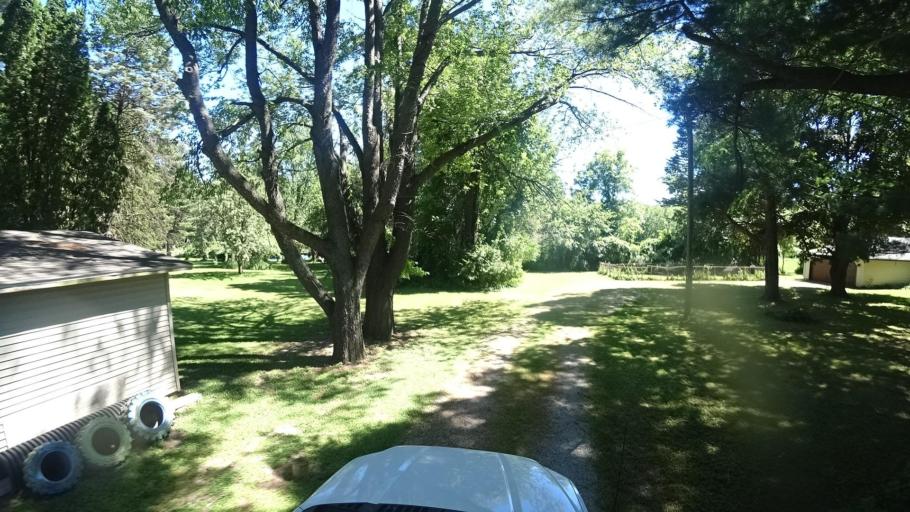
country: US
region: Indiana
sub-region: Porter County
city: Porter
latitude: 41.6247
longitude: -87.0819
